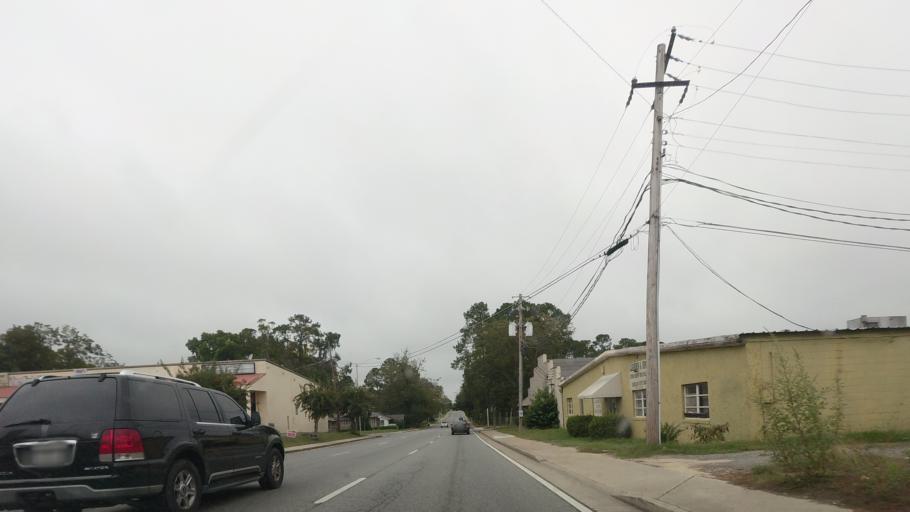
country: US
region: Georgia
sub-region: Ben Hill County
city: Fitzgerald
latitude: 31.7075
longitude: -83.2515
